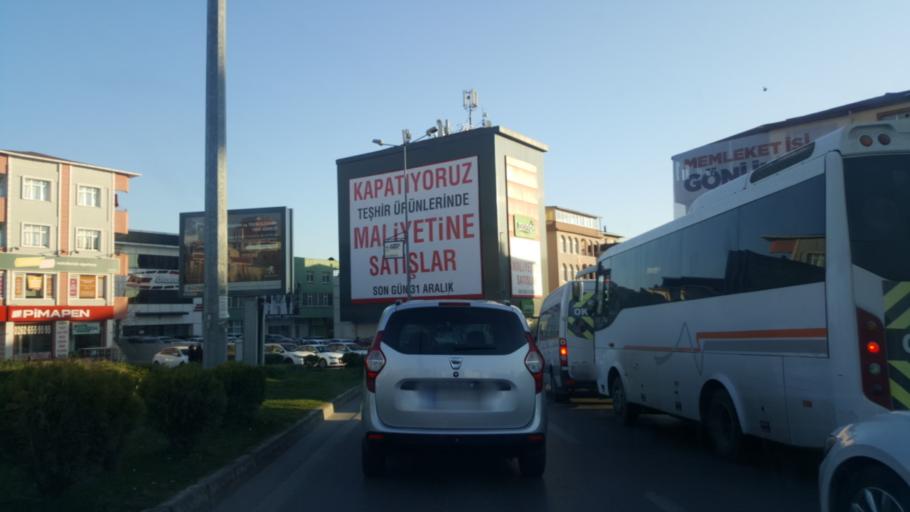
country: TR
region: Kocaeli
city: Darica
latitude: 40.7856
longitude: 29.4157
